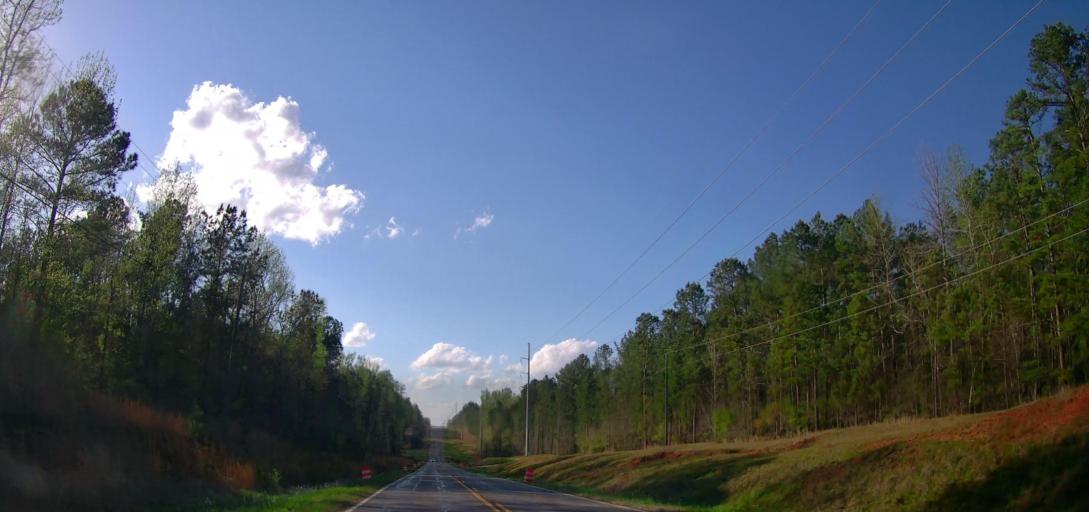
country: US
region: Georgia
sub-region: Baldwin County
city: Milledgeville
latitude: 33.1329
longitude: -83.3223
